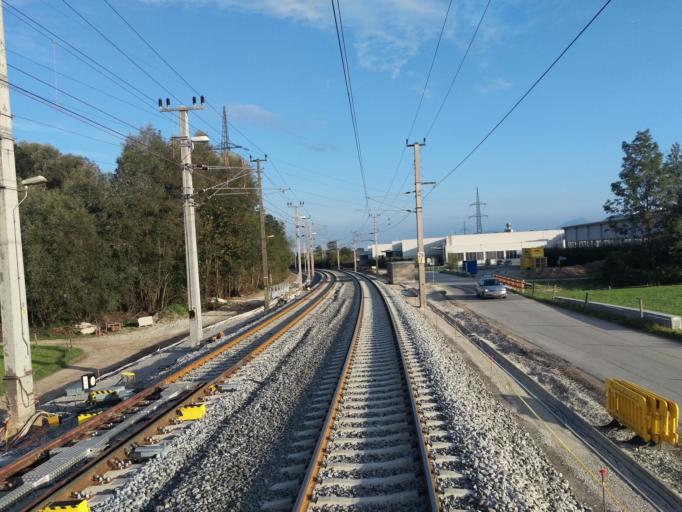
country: AT
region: Salzburg
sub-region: Politischer Bezirk Hallein
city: Golling an der Salzach
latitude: 47.6057
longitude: 13.1618
